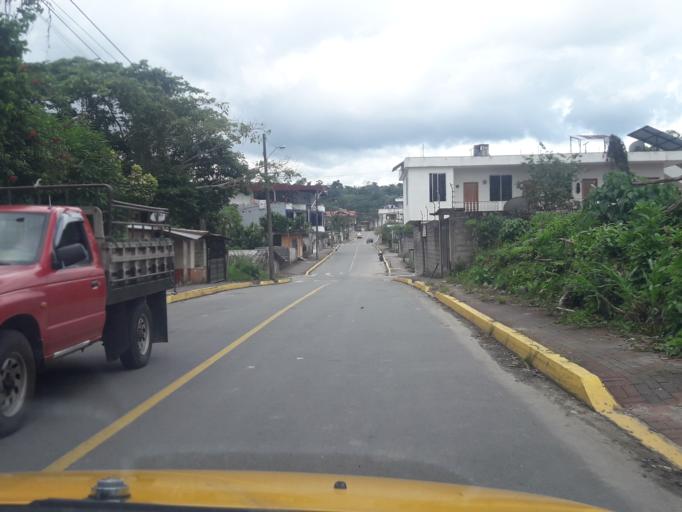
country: EC
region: Napo
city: Tena
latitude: -1.0048
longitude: -77.8168
